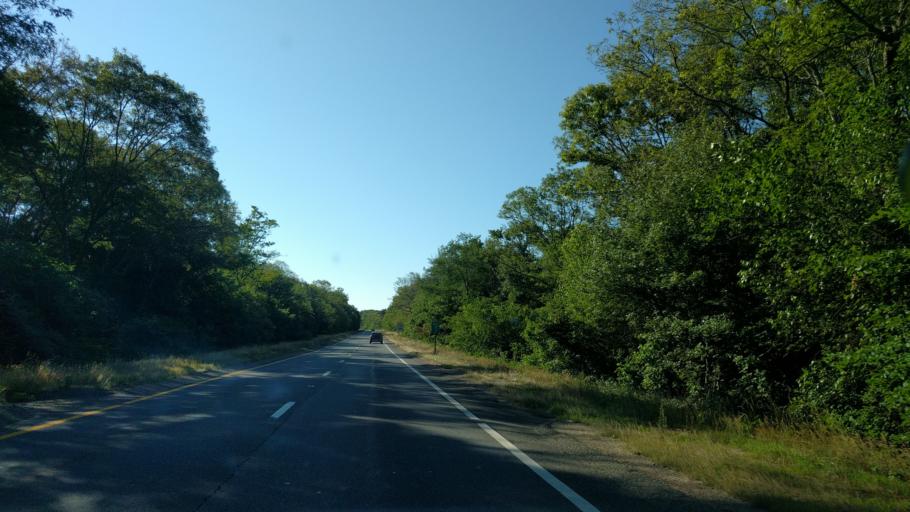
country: US
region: Massachusetts
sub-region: Barnstable County
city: West Barnstable
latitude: 41.6932
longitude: -70.3793
